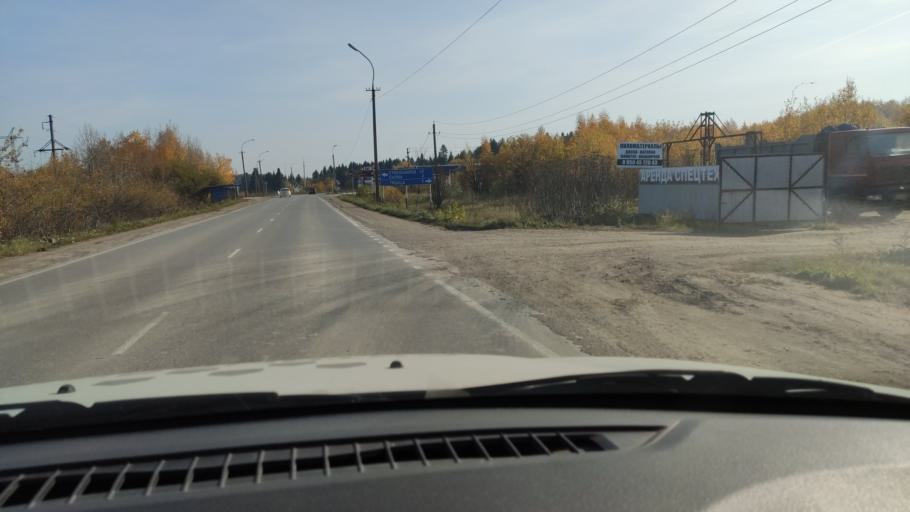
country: RU
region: Perm
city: Sylva
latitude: 58.0263
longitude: 56.7345
